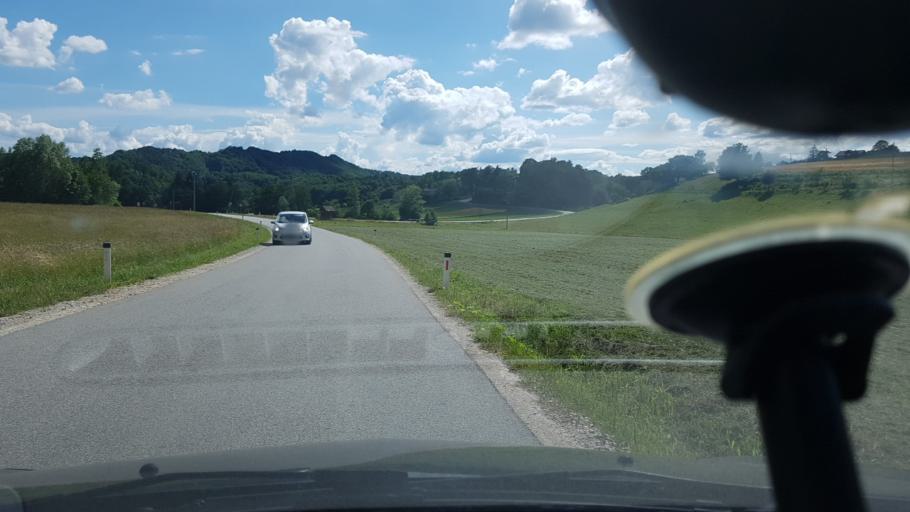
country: SI
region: Rogatec
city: Rogatec
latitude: 46.2492
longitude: 15.7293
